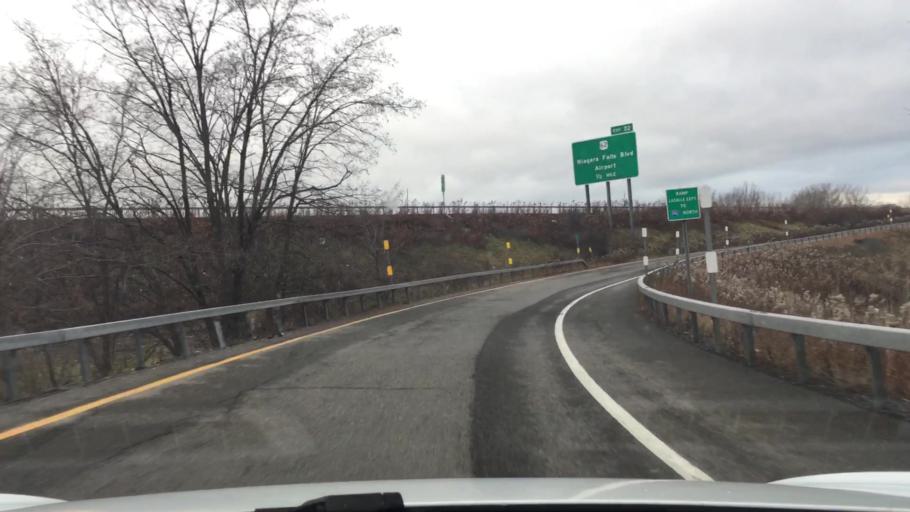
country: US
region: New York
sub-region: Niagara County
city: Niagara Falls
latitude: 43.0810
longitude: -78.9899
